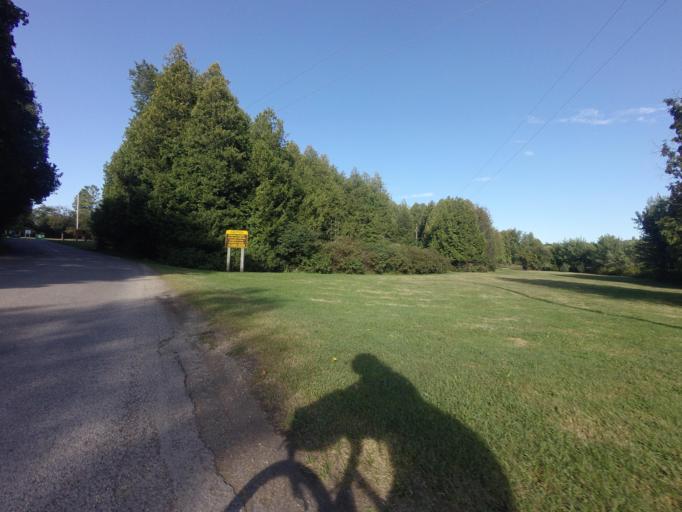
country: CA
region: Ontario
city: Waterloo
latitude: 43.6723
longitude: -80.4452
